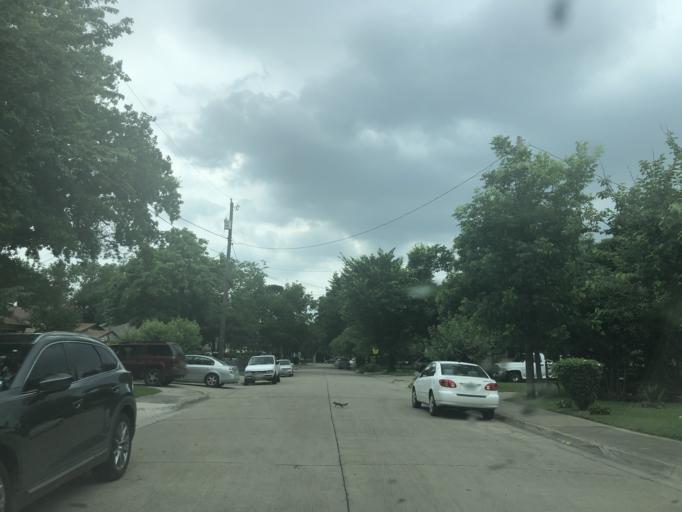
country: US
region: Texas
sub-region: Dallas County
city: Irving
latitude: 32.8103
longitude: -96.9390
